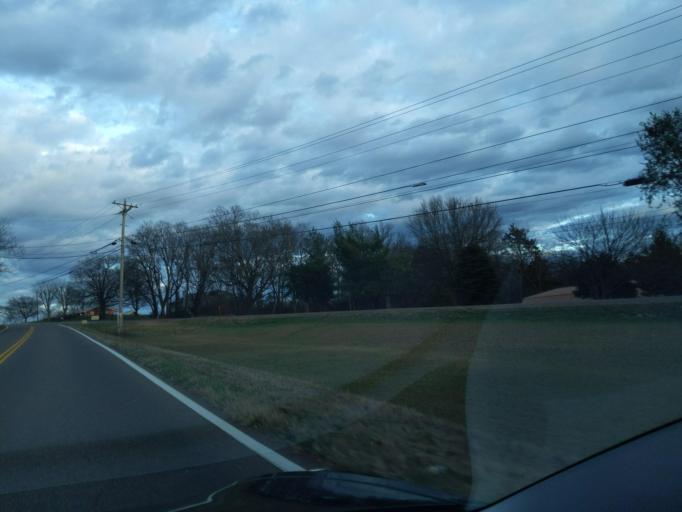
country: US
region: Tennessee
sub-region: Jefferson County
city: Dandridge
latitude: 35.9854
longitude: -83.4614
